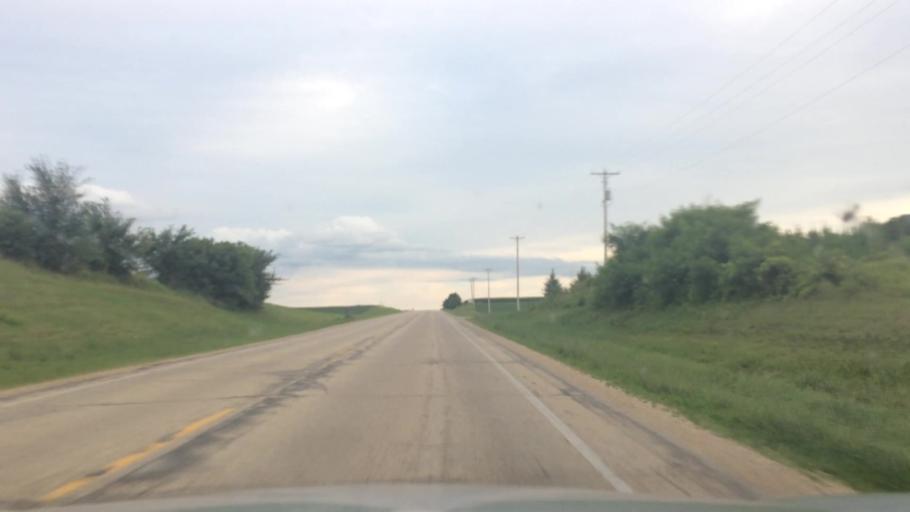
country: US
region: Wisconsin
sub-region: Columbia County
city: Lodi
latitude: 43.2463
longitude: -89.5211
